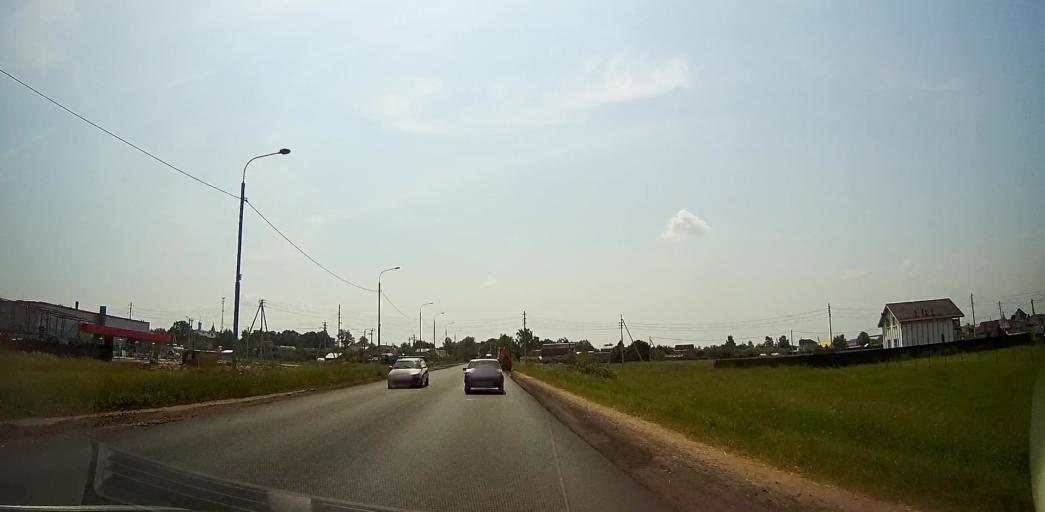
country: RU
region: Moskovskaya
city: Bronnitsy
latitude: 55.3455
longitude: 38.2230
